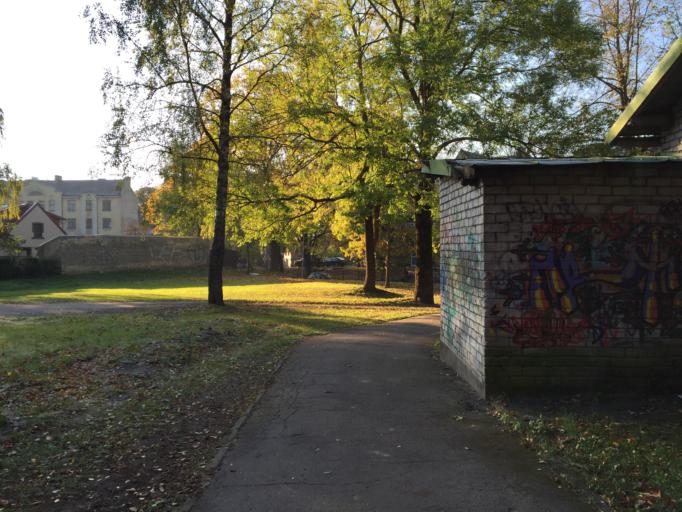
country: LV
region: Riga
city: Riga
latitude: 56.9400
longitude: 24.0695
